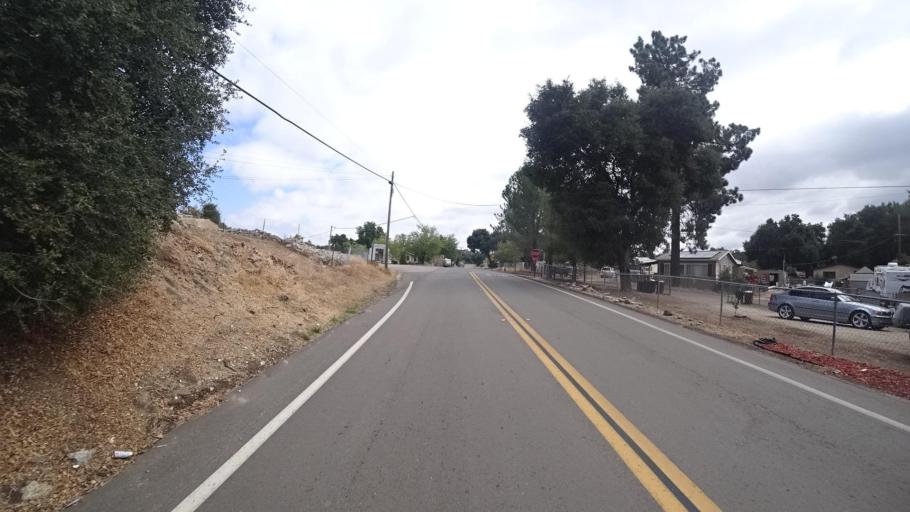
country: US
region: California
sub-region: San Diego County
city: Campo
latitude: 32.6794
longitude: -116.5112
